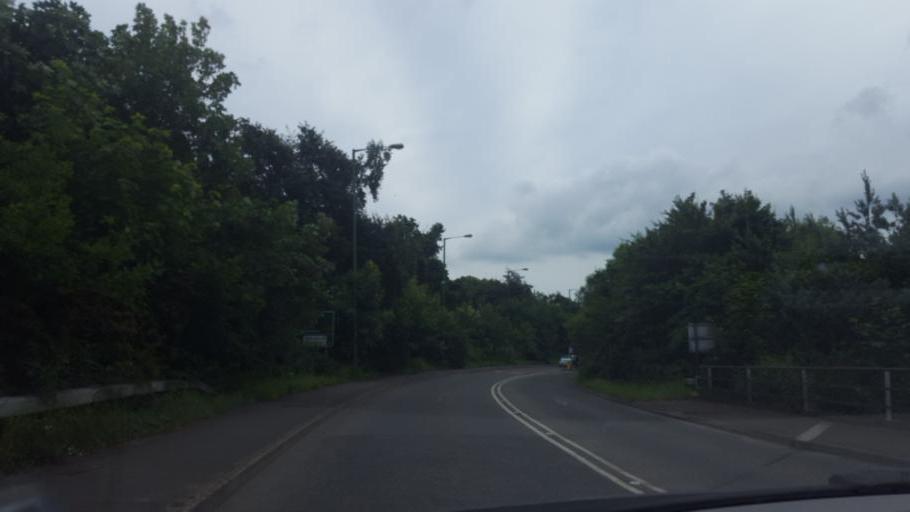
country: GB
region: England
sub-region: Royal Borough of Windsor and Maidenhead
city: Bisham
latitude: 51.5300
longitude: -0.7846
